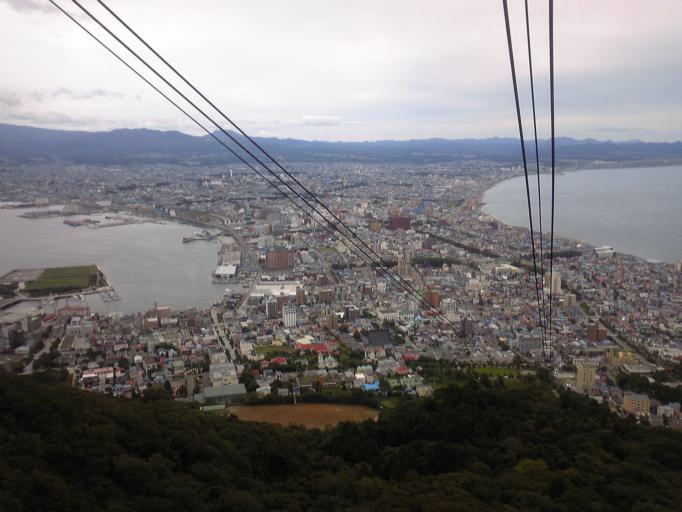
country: JP
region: Hokkaido
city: Hakodate
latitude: 41.7607
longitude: 140.7139
